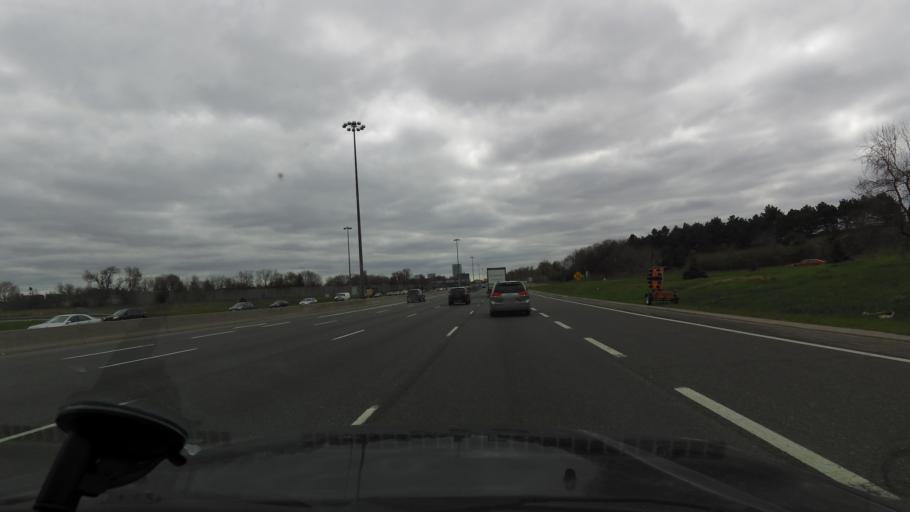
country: CA
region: Ontario
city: Willowdale
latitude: 43.7948
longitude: -79.3439
